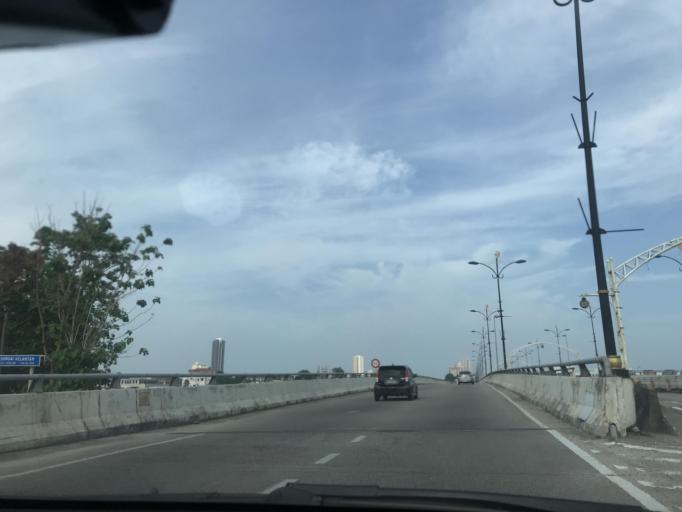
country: MY
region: Kelantan
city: Kota Bharu
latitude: 6.1168
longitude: 102.2264
